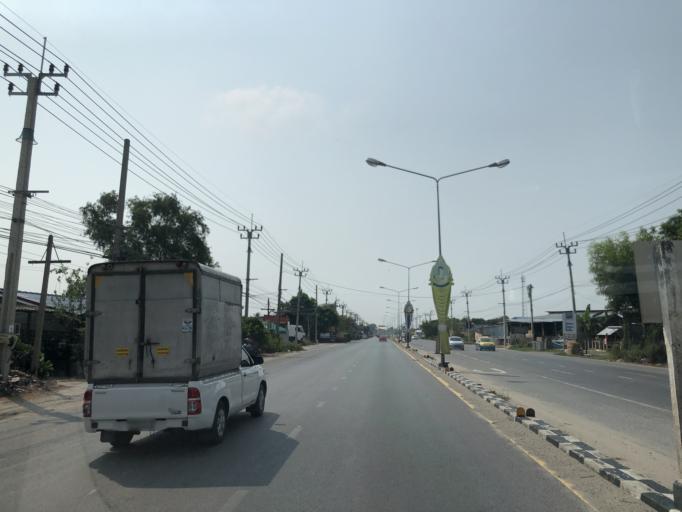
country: TH
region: Samut Prakan
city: Bang Bo District
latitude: 13.5223
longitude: 100.7884
